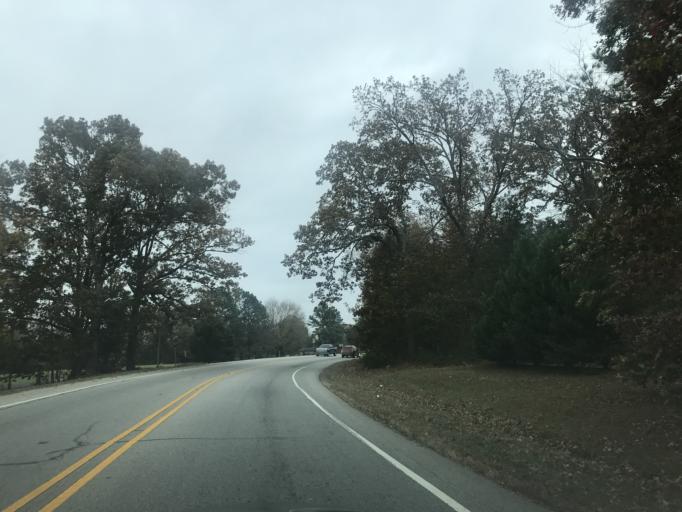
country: US
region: North Carolina
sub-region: Franklin County
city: Youngsville
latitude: 36.0288
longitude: -78.4801
